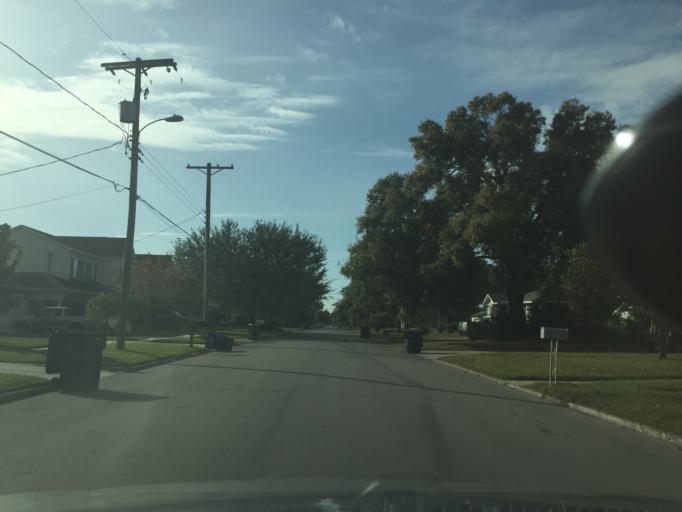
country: US
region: Florida
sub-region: Hillsborough County
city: Tampa
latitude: 27.9459
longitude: -82.4904
